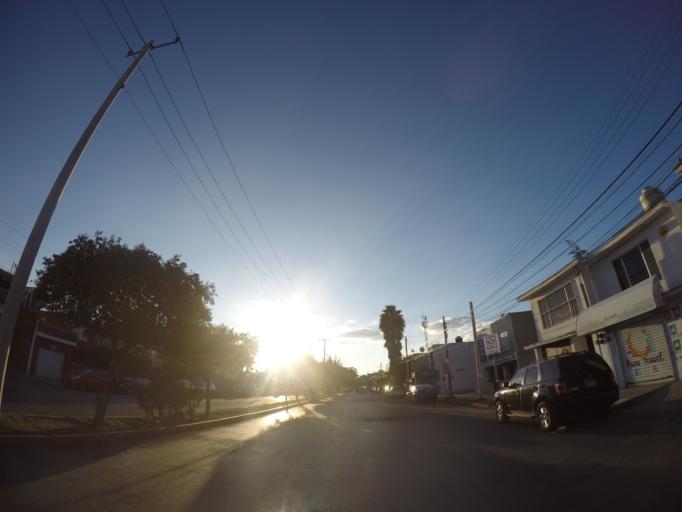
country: MX
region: San Luis Potosi
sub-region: San Luis Potosi
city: San Luis Potosi
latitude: 22.1384
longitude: -100.9867
